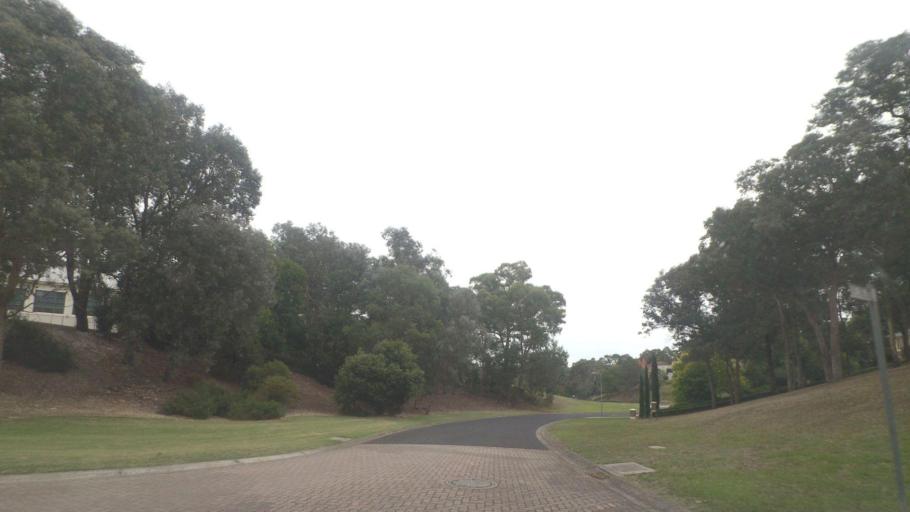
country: AU
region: Victoria
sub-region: Nillumbik
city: North Warrandyte
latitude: -37.7521
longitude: 145.1917
